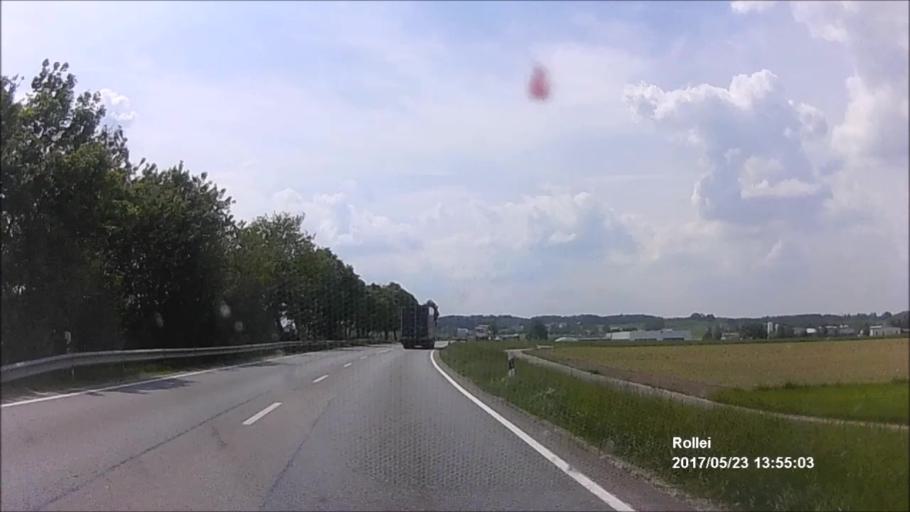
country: DE
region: Bavaria
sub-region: Upper Bavaria
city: Haag in Oberbayern
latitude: 48.1664
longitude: 12.1513
